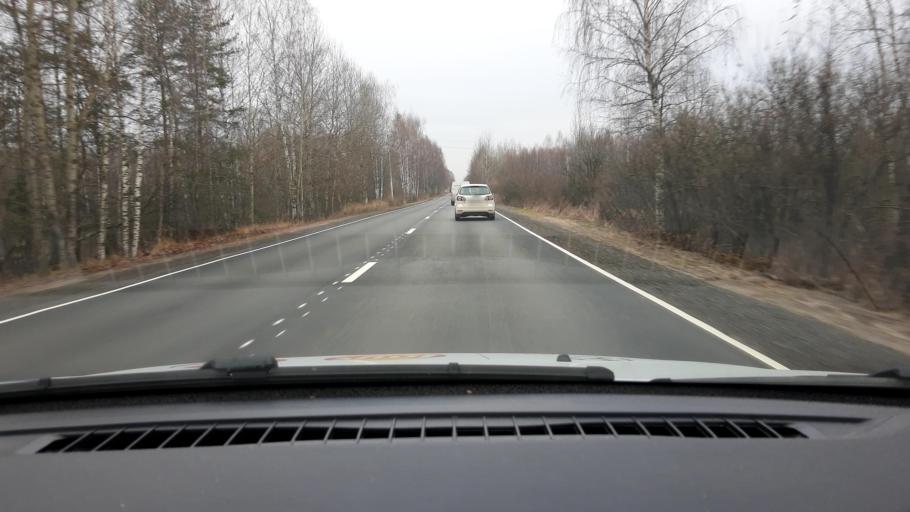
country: RU
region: Nizjnij Novgorod
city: Novaya Balakhna
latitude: 56.5619
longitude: 43.7272
